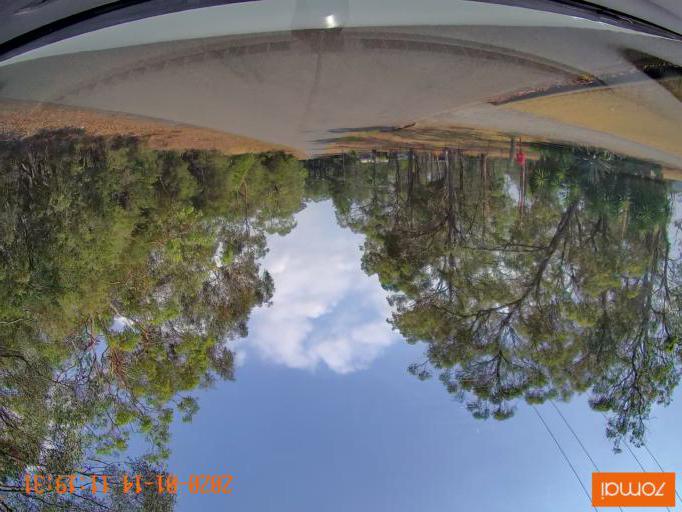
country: AU
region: New South Wales
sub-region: Lake Macquarie Shire
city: Cooranbong
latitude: -33.0983
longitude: 151.4602
